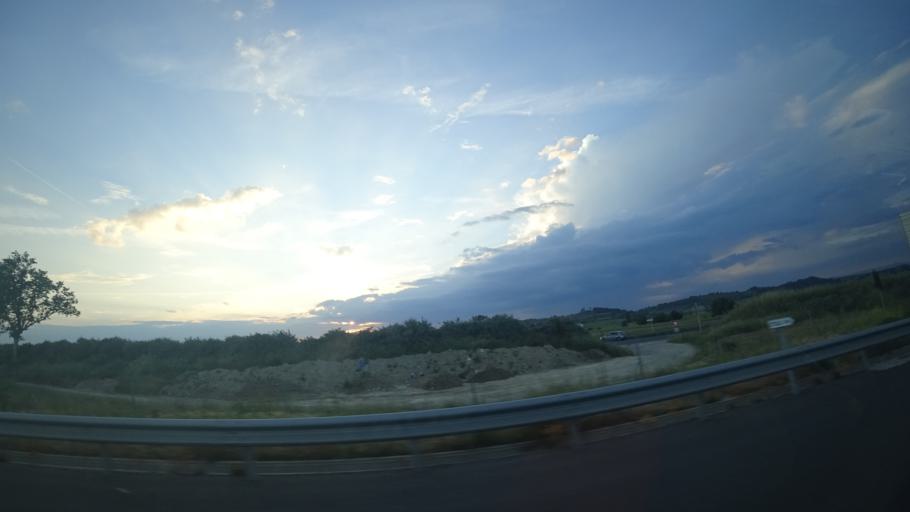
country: FR
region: Languedoc-Roussillon
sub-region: Departement de l'Herault
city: Tourbes
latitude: 43.4410
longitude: 3.3955
